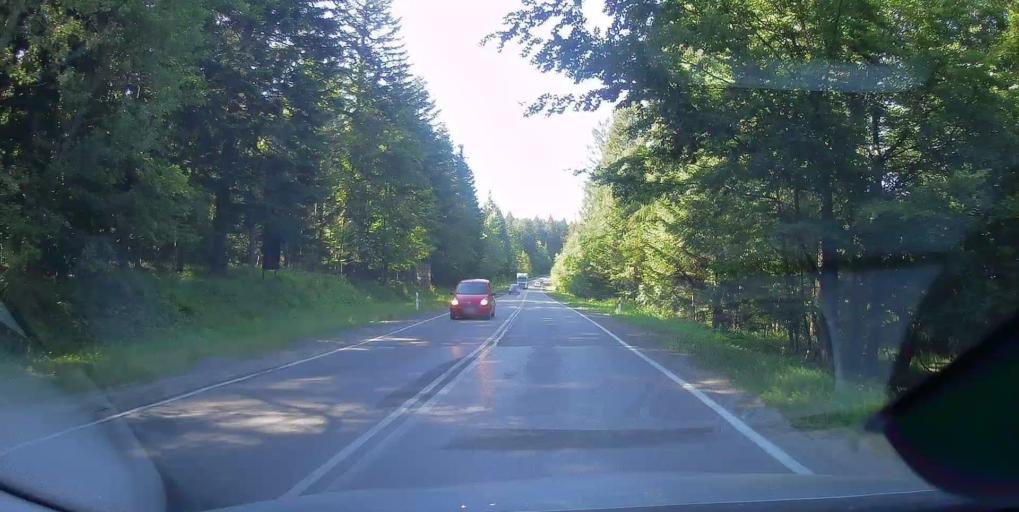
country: PL
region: Lesser Poland Voivodeship
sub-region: Powiat nowosadecki
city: Krynica-Zdroj
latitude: 49.4519
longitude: 20.9534
